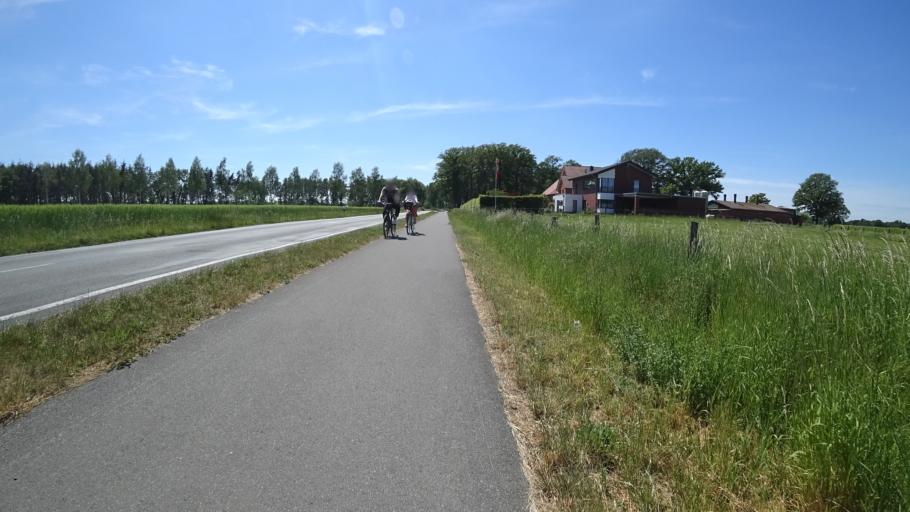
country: DE
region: North Rhine-Westphalia
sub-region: Regierungsbezirk Detmold
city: Rheda-Wiedenbruck
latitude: 51.8446
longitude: 8.3459
